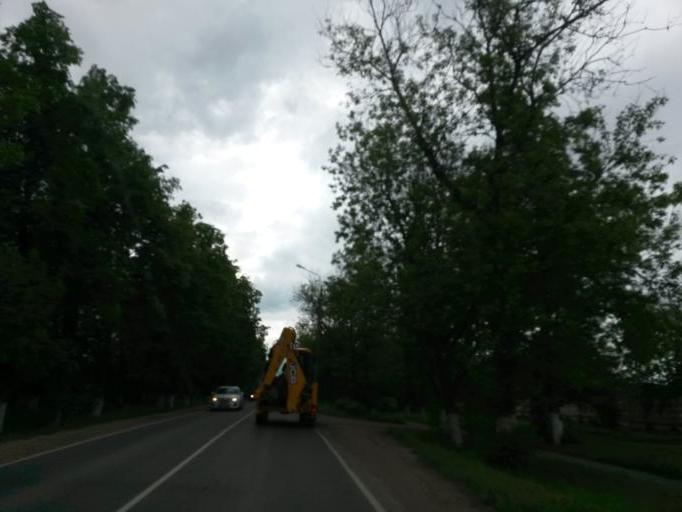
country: RU
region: Moskovskaya
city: Klimovsk
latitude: 55.3495
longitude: 37.5456
